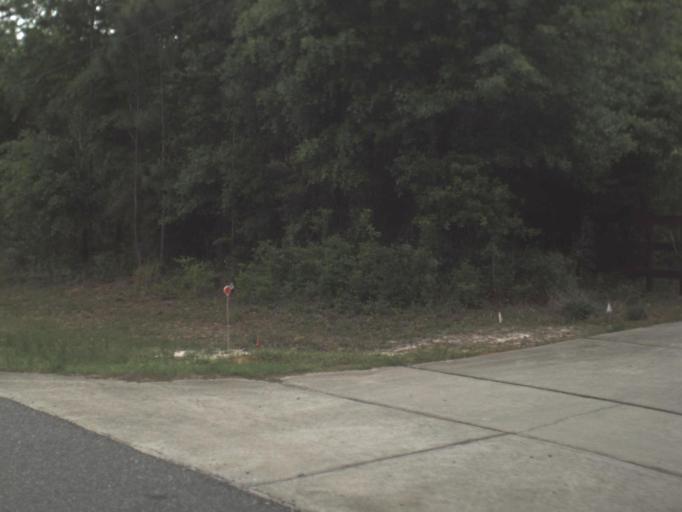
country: US
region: Florida
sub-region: Santa Rosa County
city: Point Baker
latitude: 30.7249
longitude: -87.0446
